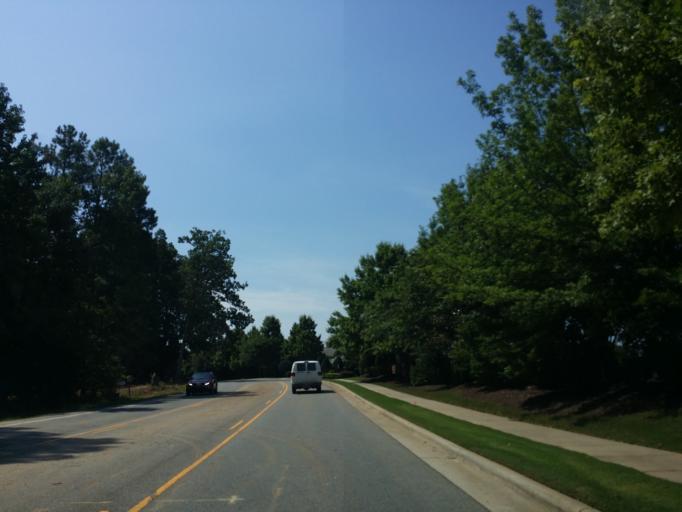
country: US
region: North Carolina
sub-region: Wake County
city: Cary
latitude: 35.8828
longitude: -78.7275
